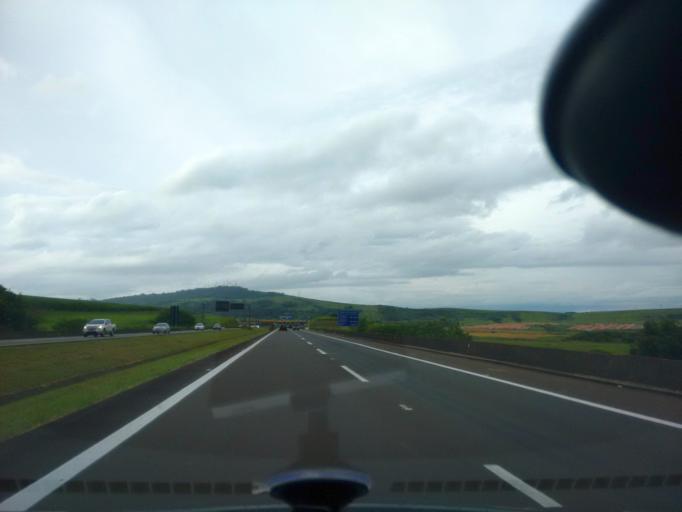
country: BR
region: Sao Paulo
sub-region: Limeira
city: Limeira
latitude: -22.5616
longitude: -47.4588
